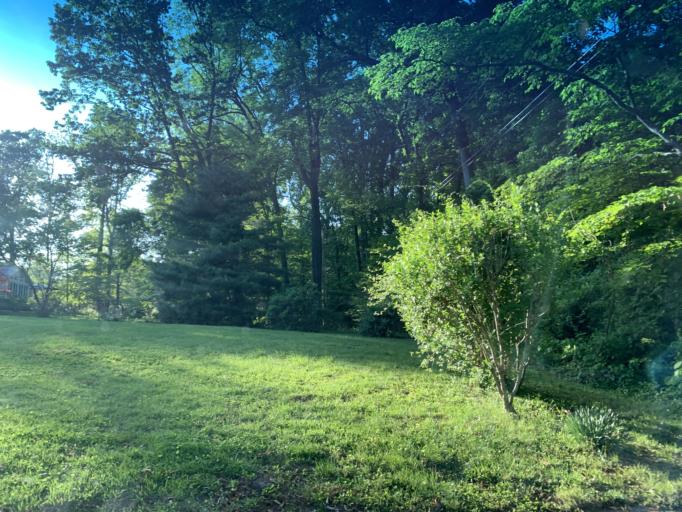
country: US
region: Maryland
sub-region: Harford County
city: Bel Air South
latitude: 39.5102
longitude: -76.2893
